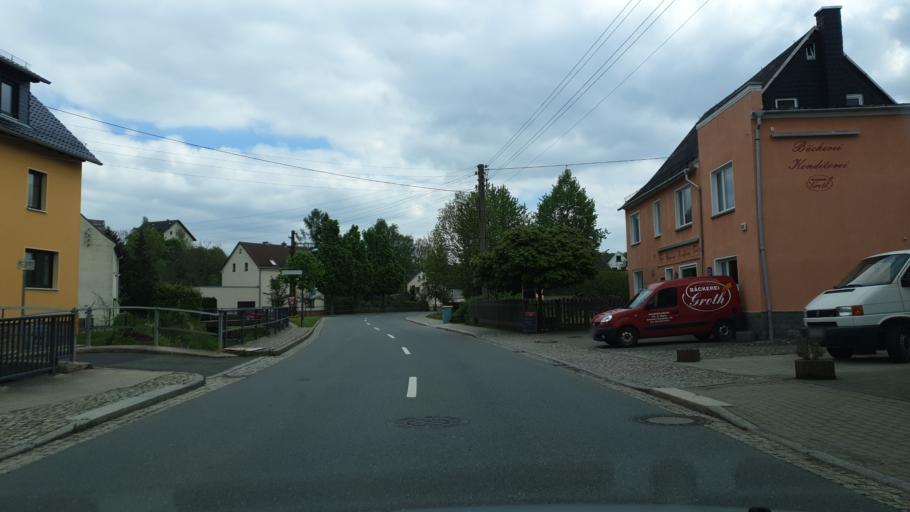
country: DE
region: Saxony
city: Oberlungwitz
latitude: 50.7663
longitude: 12.7069
